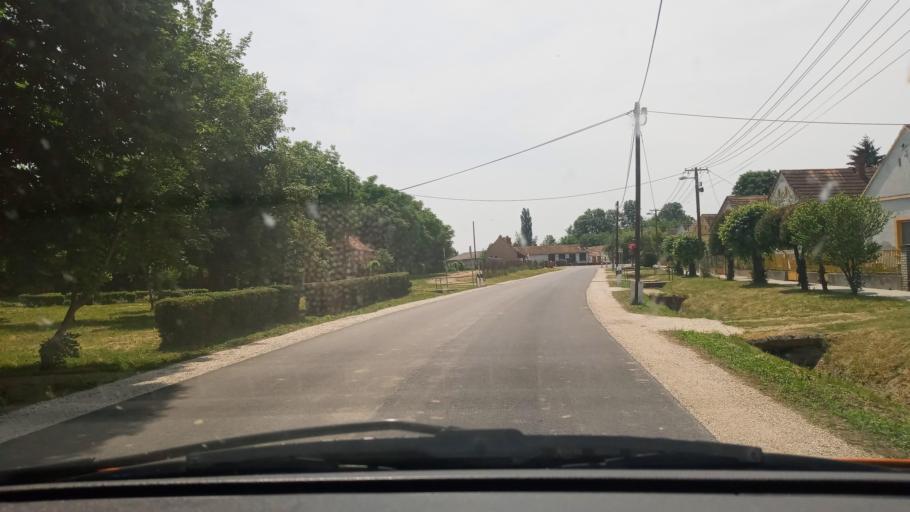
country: HU
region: Baranya
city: Szigetvar
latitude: 45.9613
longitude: 17.6589
